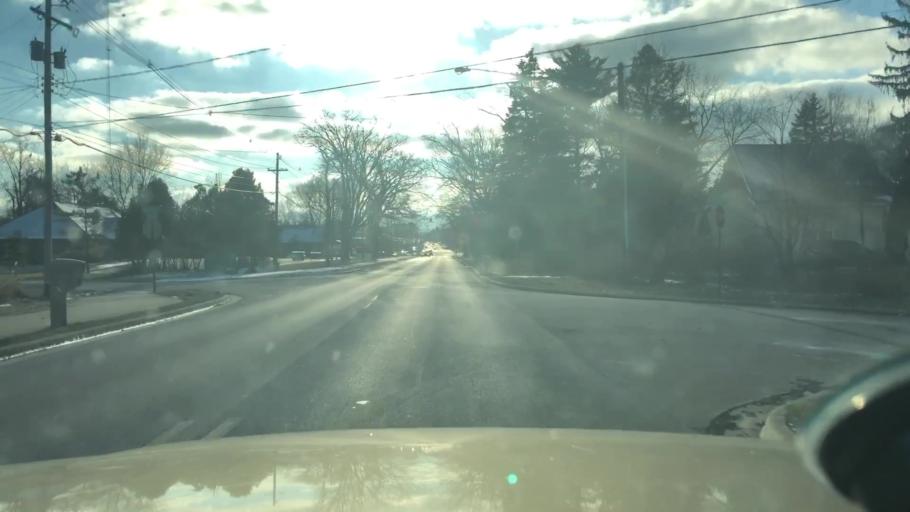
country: US
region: Michigan
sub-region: Jackson County
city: Vandercook Lake
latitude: 42.2070
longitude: -84.4301
